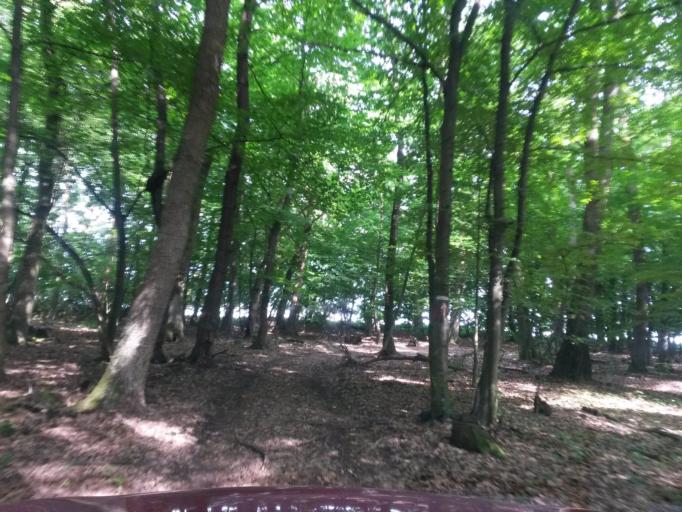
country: SK
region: Kosicky
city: Moldava nad Bodvou
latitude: 48.6378
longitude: 21.1030
